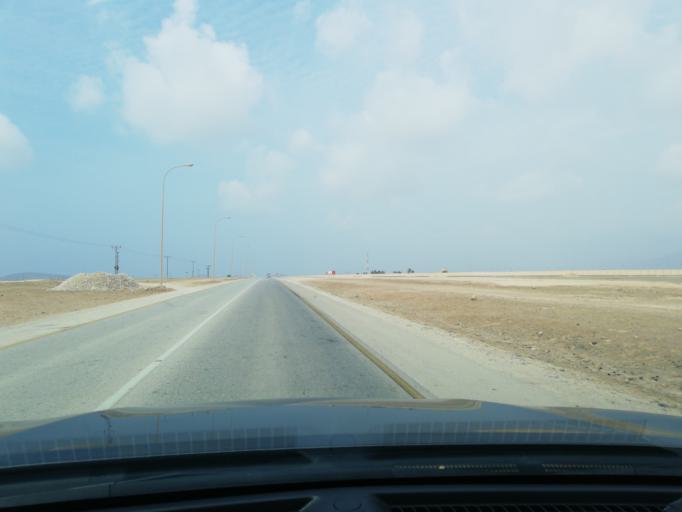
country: OM
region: Zufar
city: Salalah
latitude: 16.9437
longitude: 53.8486
